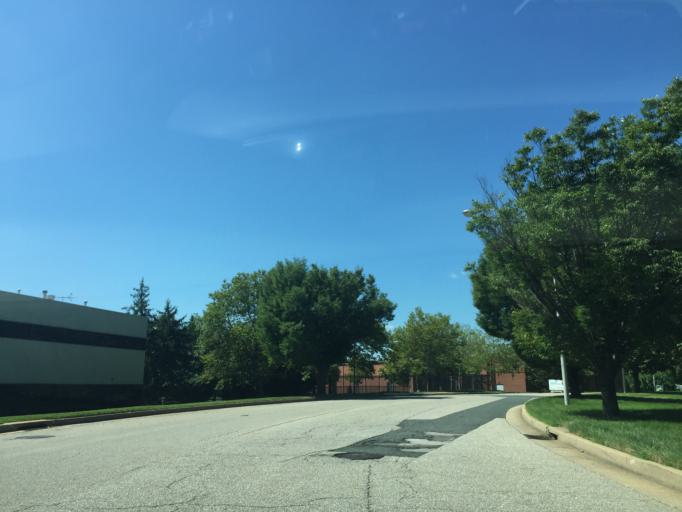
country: US
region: Maryland
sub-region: Baltimore County
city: Dundalk
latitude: 39.2680
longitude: -76.5326
